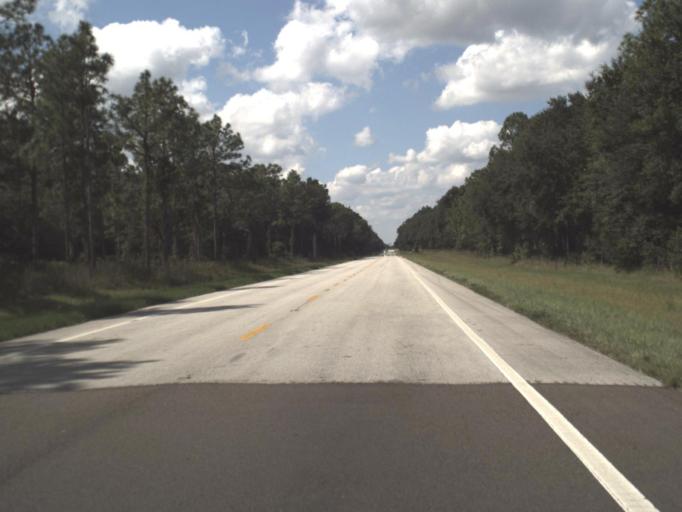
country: US
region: Florida
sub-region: Highlands County
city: Sebring
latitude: 27.4124
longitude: -81.5372
